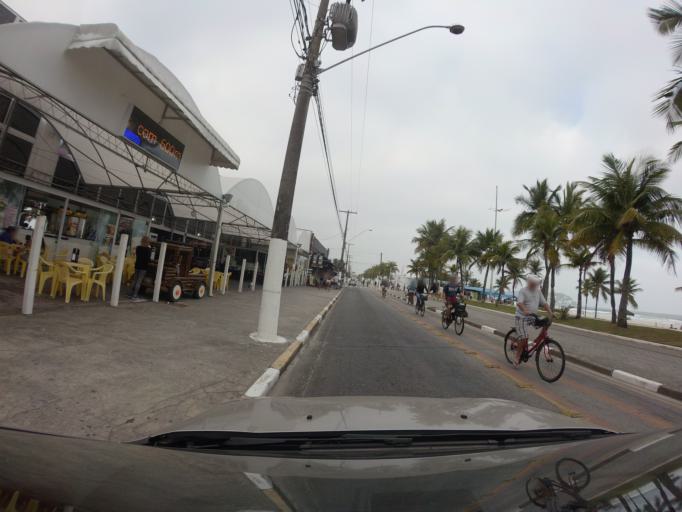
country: BR
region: Sao Paulo
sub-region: Guaruja
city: Guaruja
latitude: -23.9876
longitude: -46.2336
